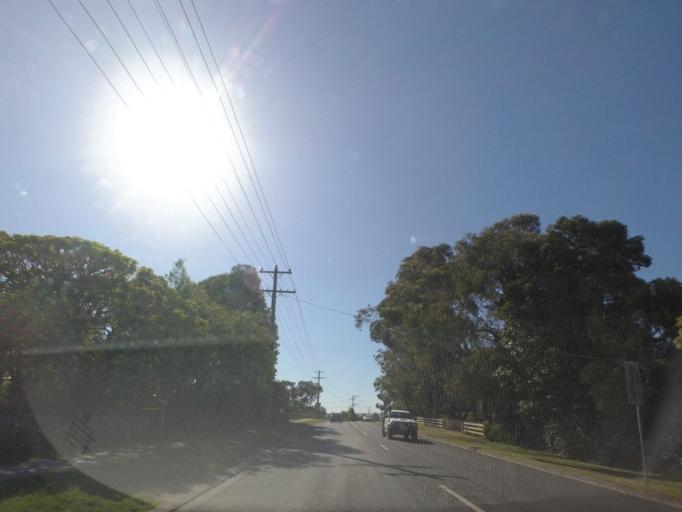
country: AU
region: Victoria
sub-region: Yarra Ranges
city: Yarra Junction
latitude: -37.7916
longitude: 145.6228
